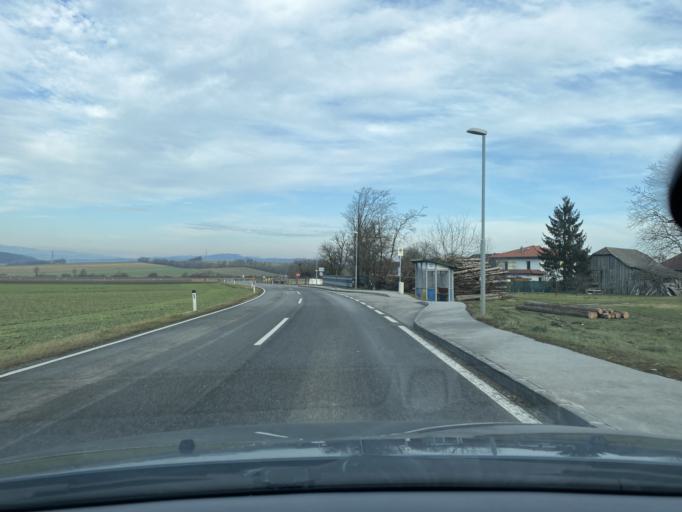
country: AT
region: Lower Austria
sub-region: Politischer Bezirk Melk
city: Loosdorf
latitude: 48.1795
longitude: 15.3779
